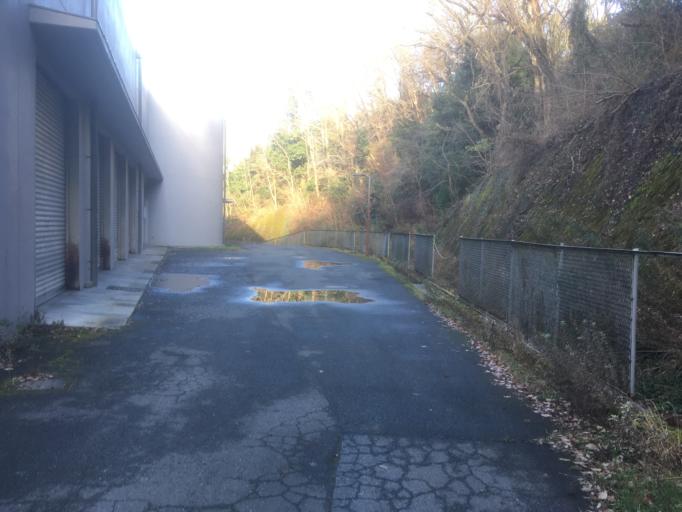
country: JP
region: Nara
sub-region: Ikoma-shi
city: Ikoma
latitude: 34.6952
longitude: 135.6752
